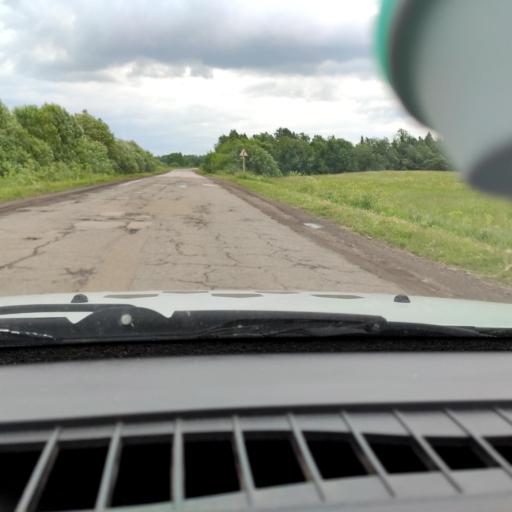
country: RU
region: Perm
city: Uinskoye
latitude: 57.1651
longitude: 56.5677
